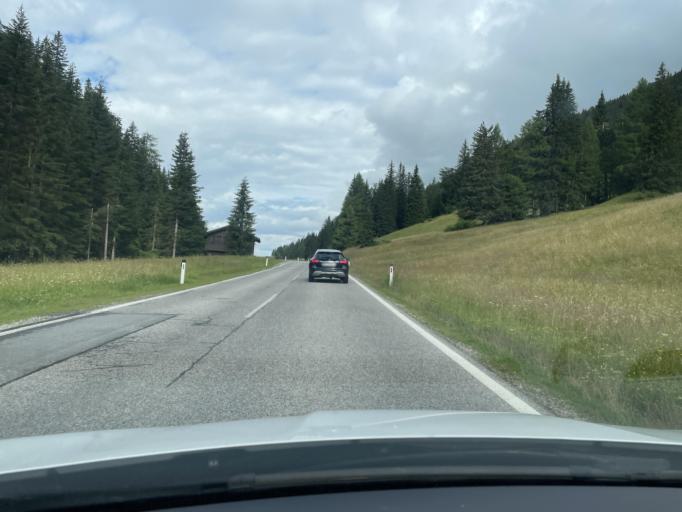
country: AT
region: Tyrol
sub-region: Politischer Bezirk Lienz
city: Abfaltersbach
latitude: 46.7171
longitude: 12.5449
